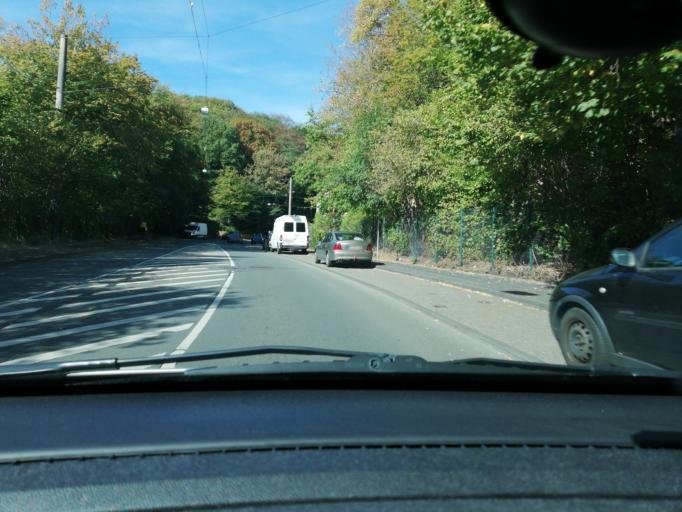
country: DE
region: North Rhine-Westphalia
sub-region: Regierungsbezirk Dusseldorf
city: Wuppertal
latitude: 51.2855
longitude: 7.2073
